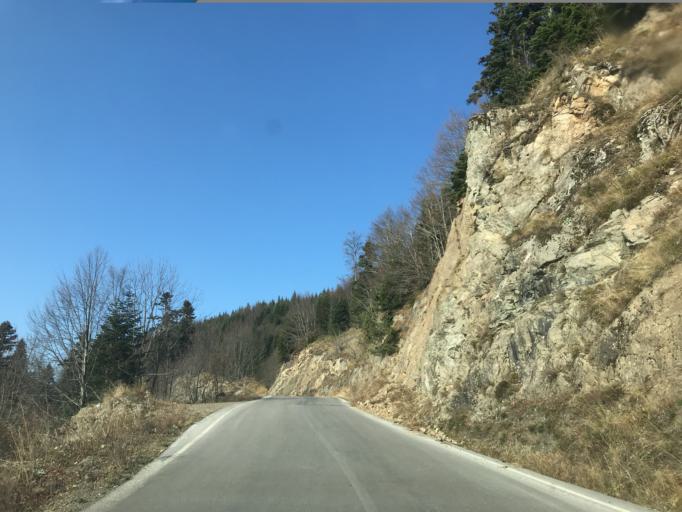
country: TR
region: Bolu
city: Bolu
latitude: 40.8852
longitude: 31.6825
